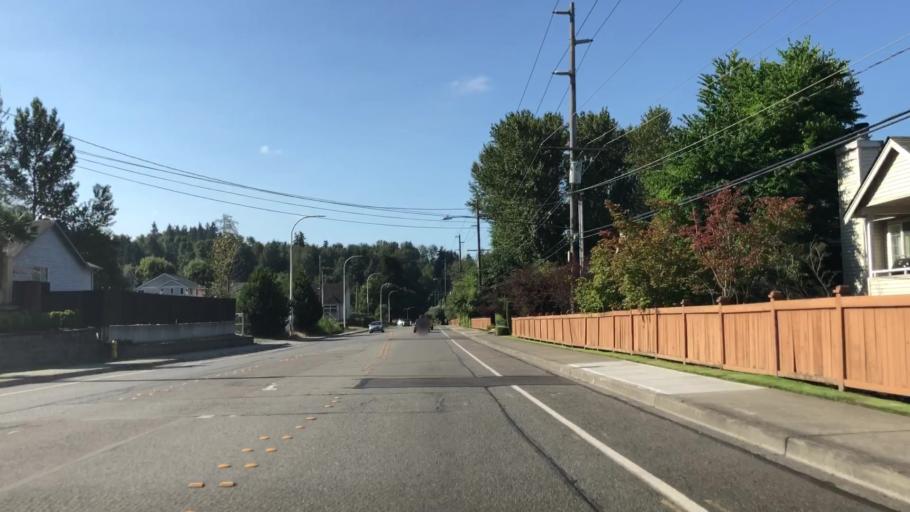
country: US
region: Washington
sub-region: King County
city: East Hill-Meridian
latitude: 47.4327
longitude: -122.2130
